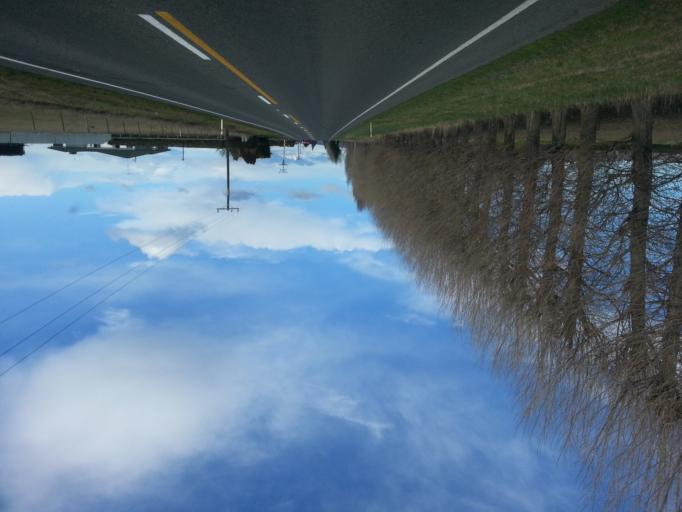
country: NZ
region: Canterbury
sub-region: Hurunui District
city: Amberley
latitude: -42.7795
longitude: 172.8438
